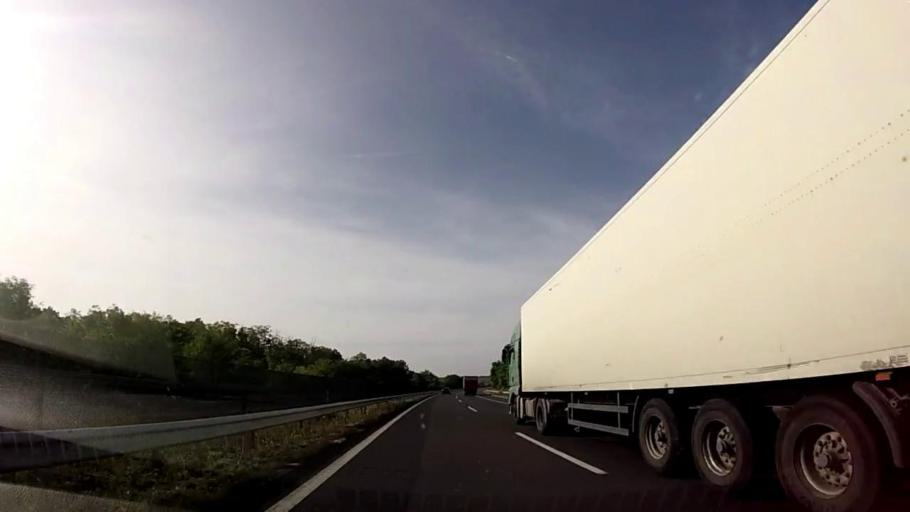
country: HU
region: Somogy
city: Zamardi
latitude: 46.8354
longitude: 17.9484
